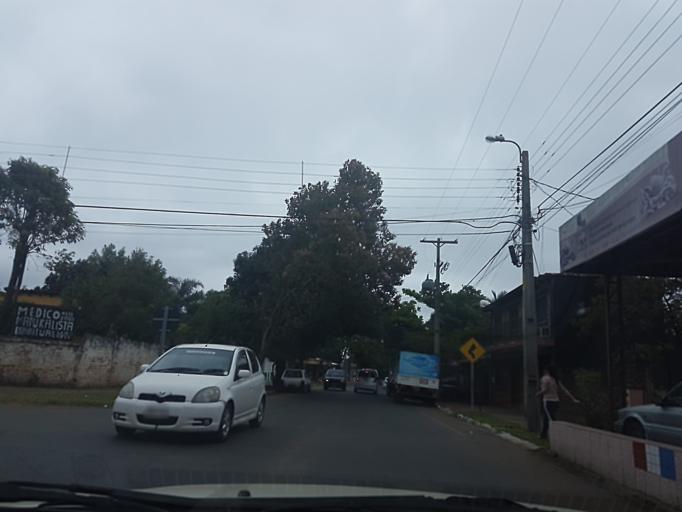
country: PY
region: Central
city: Lambare
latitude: -25.3328
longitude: -57.5710
